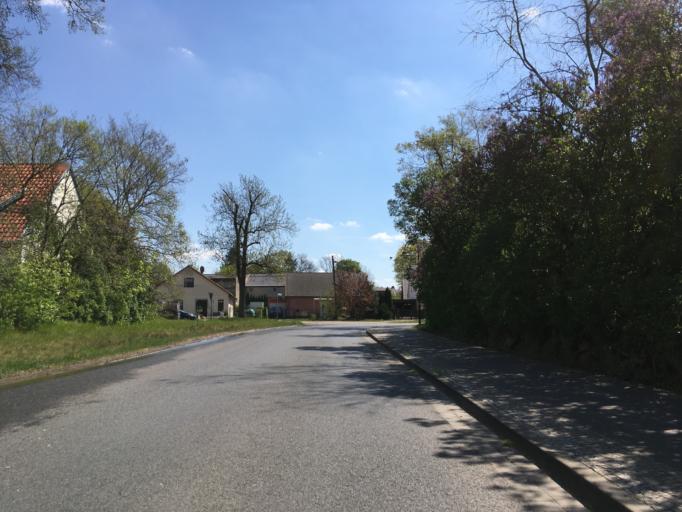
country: DE
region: Brandenburg
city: Bernau bei Berlin
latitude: 52.6643
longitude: 13.6372
